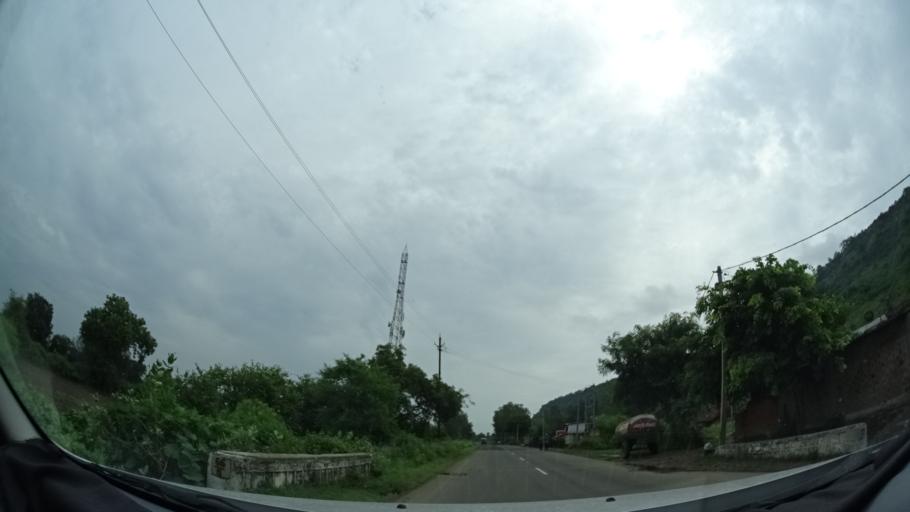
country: IN
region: Madhya Pradesh
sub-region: Raisen
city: Sultanpur
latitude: 23.3034
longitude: 77.9708
